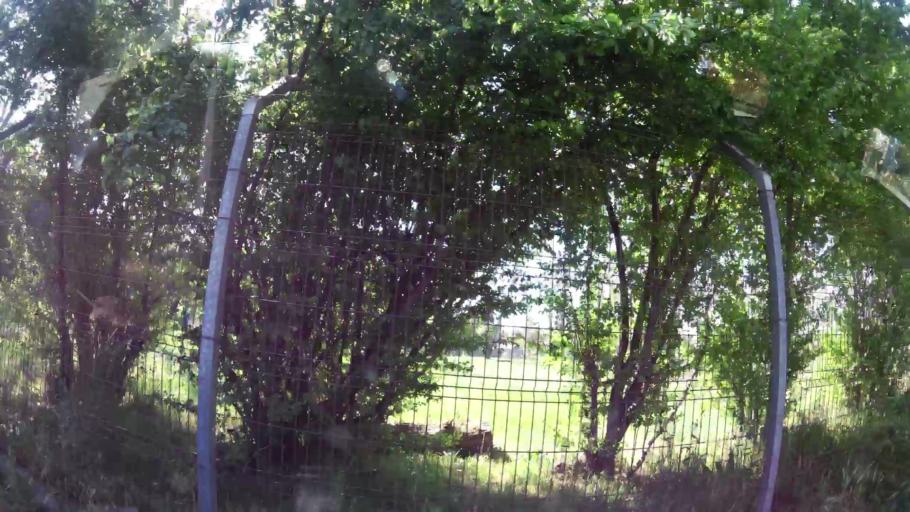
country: CL
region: Santiago Metropolitan
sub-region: Provincia de Santiago
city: La Pintana
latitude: -33.5635
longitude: -70.6296
